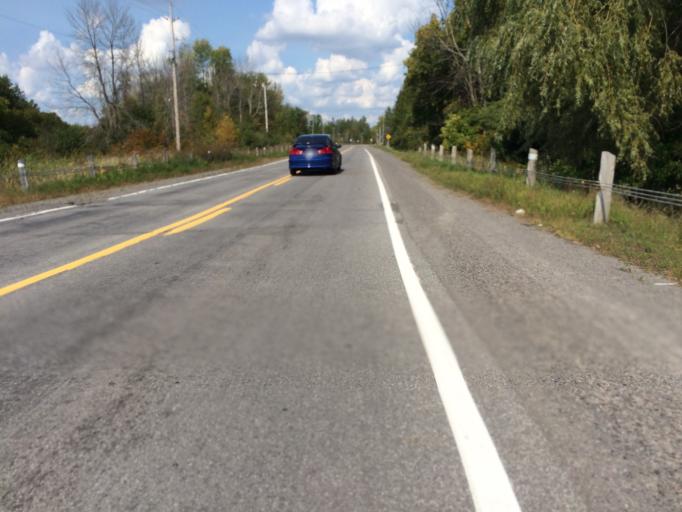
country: CA
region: Ontario
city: Bells Corners
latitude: 45.1721
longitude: -75.6400
